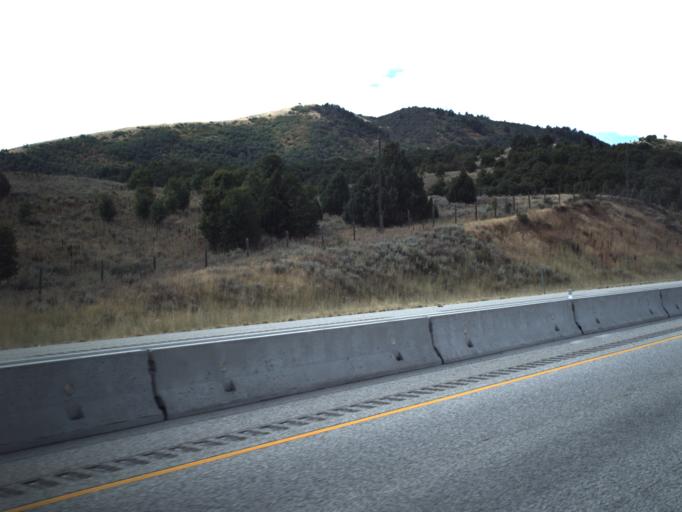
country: US
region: Utah
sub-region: Box Elder County
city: Brigham City
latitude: 41.5291
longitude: -111.9527
